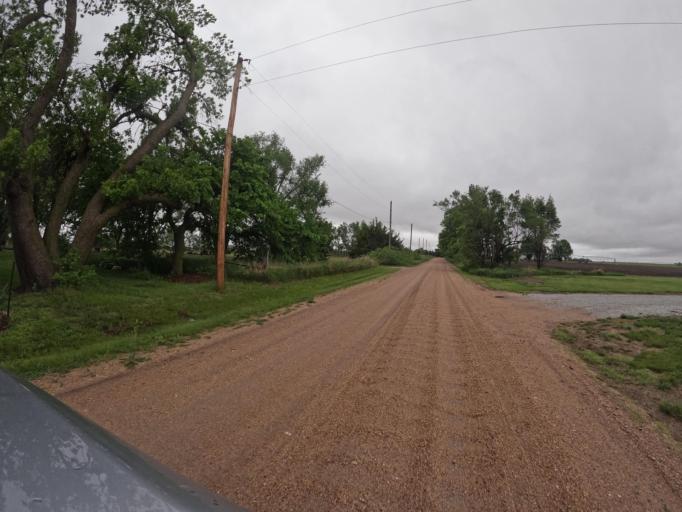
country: US
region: Nebraska
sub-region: Clay County
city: Harvard
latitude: 40.6289
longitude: -98.0968
